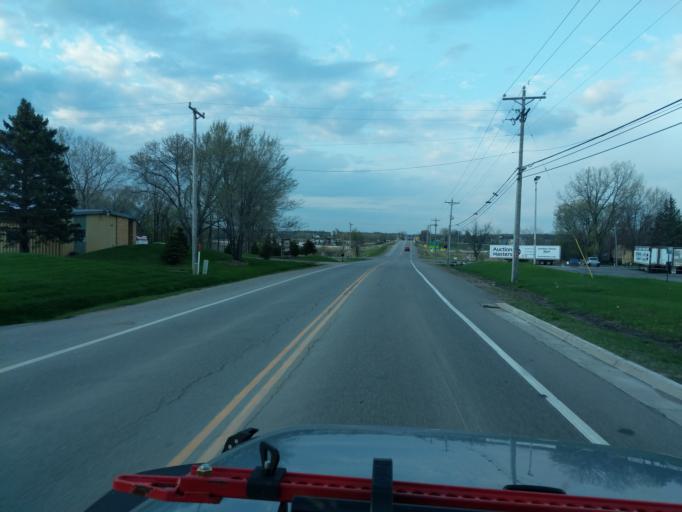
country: US
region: Minnesota
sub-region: Hennepin County
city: Rogers
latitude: 45.1673
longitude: -93.5216
